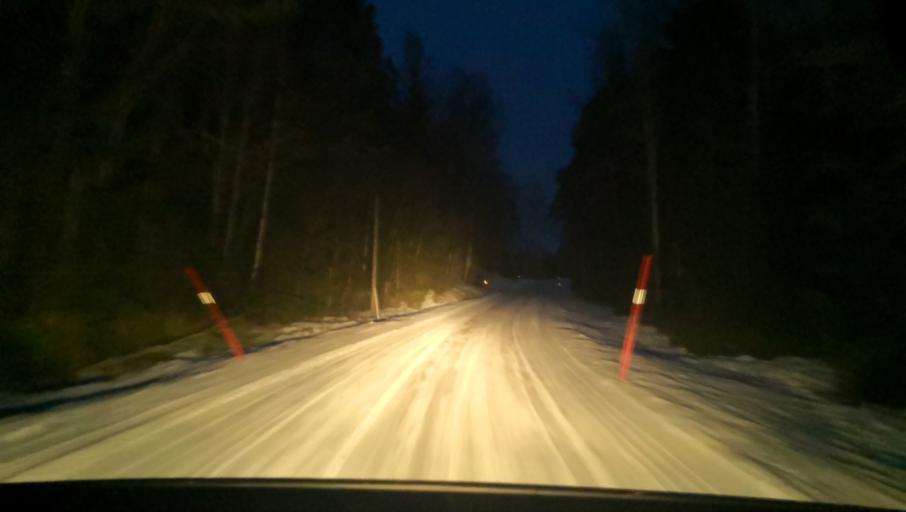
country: SE
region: Uppsala
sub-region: Heby Kommun
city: Tarnsjo
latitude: 60.2614
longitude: 16.7812
